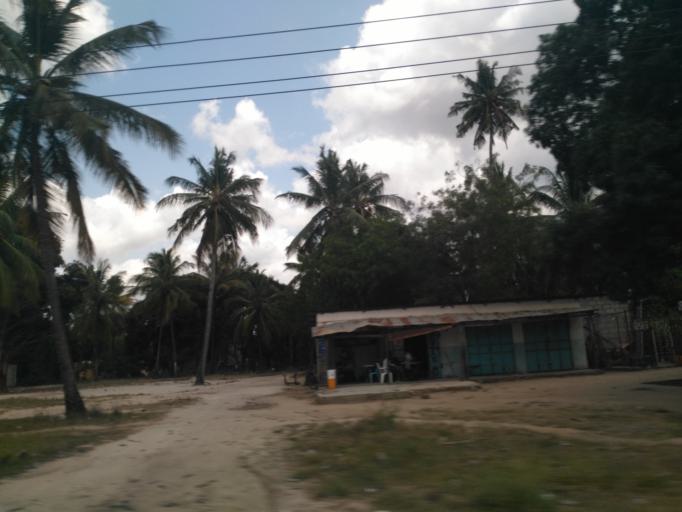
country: TZ
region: Dar es Salaam
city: Dar es Salaam
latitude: -6.8676
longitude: 39.3498
